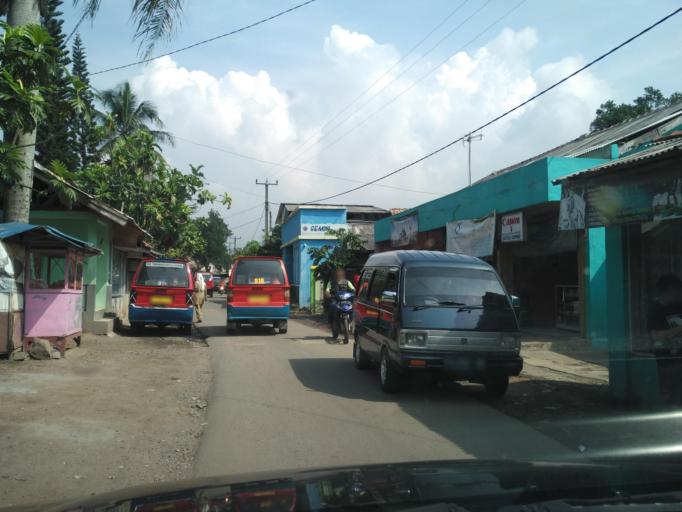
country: ID
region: West Java
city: Ciranjang-hilir
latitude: -6.7964
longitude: 107.1596
